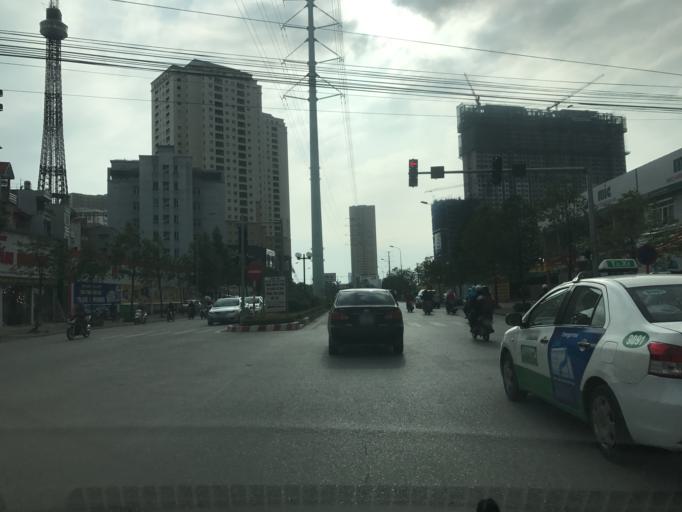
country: VN
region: Ha Noi
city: Thanh Xuan
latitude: 20.9949
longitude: 105.7903
